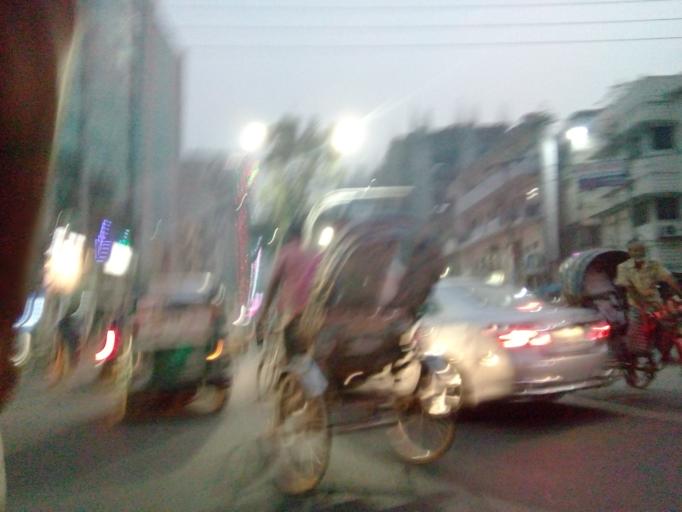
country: BD
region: Dhaka
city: Paltan
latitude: 23.7370
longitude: 90.4103
